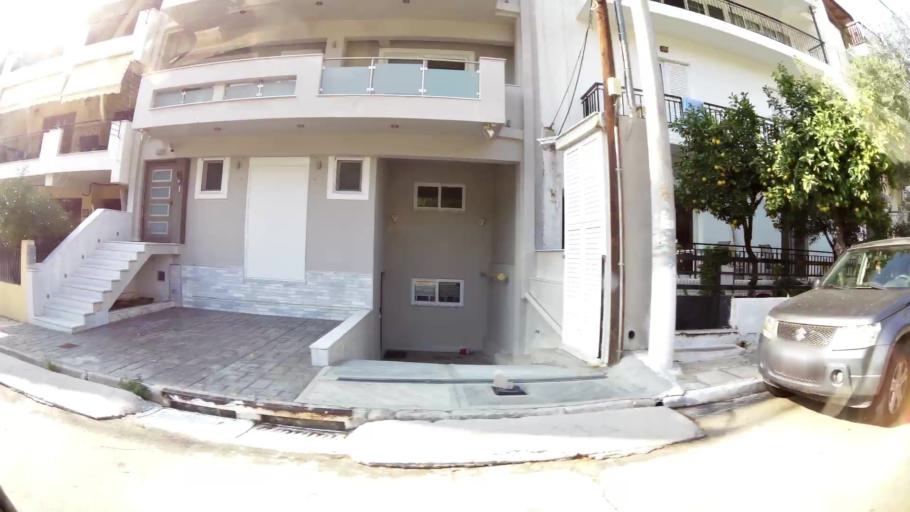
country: GR
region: Attica
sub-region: Nomarchia Athinas
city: Argyroupoli
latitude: 37.9037
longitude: 23.7570
